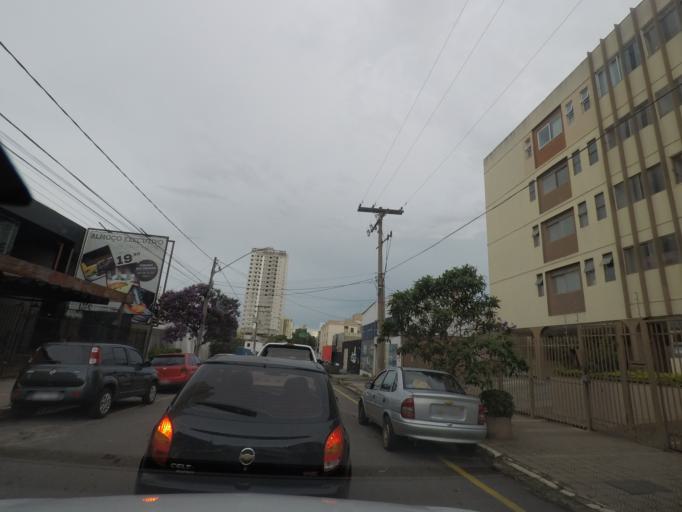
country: BR
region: Goias
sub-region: Goiania
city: Goiania
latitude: -16.7054
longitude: -49.2632
